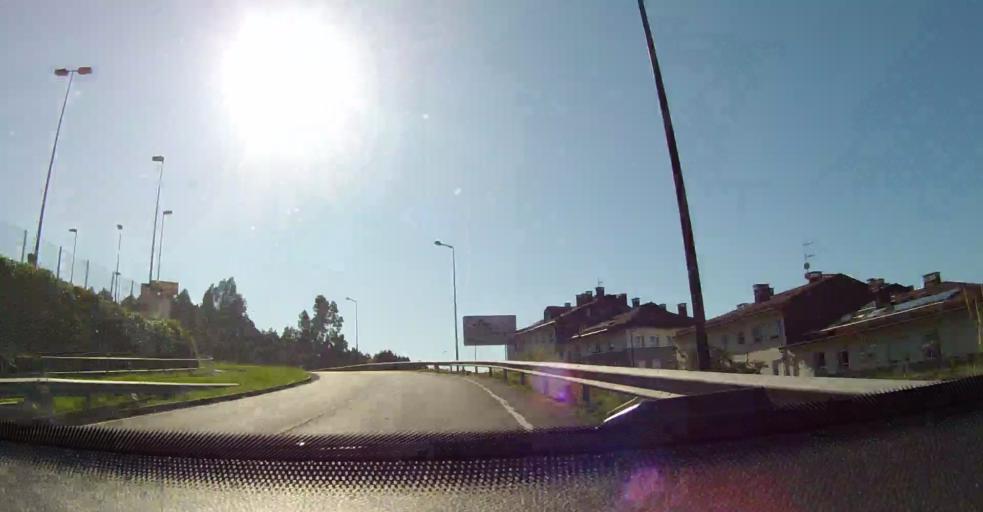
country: ES
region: Asturias
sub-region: Province of Asturias
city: Ribadesella
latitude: 43.4655
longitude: -5.0880
